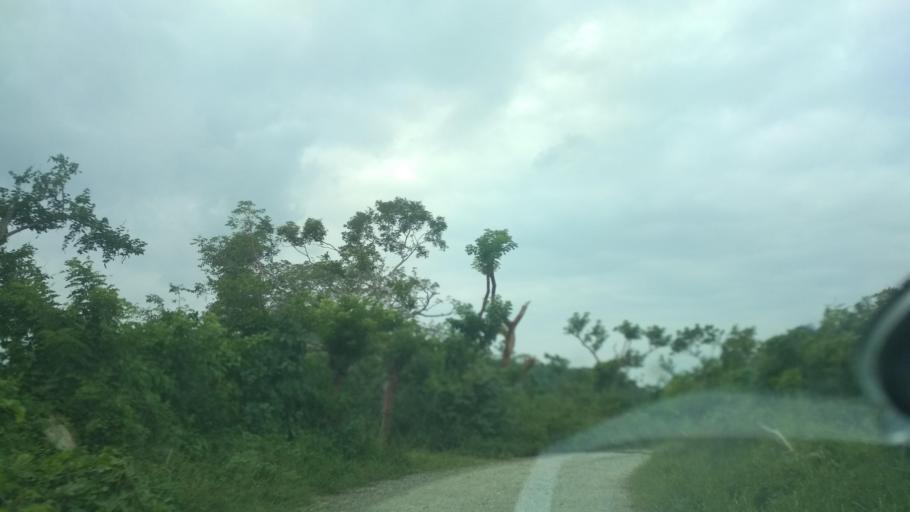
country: MX
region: Veracruz
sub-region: Poza Rica de Hidalgo
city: El Mollejon
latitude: 20.5223
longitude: -97.3884
